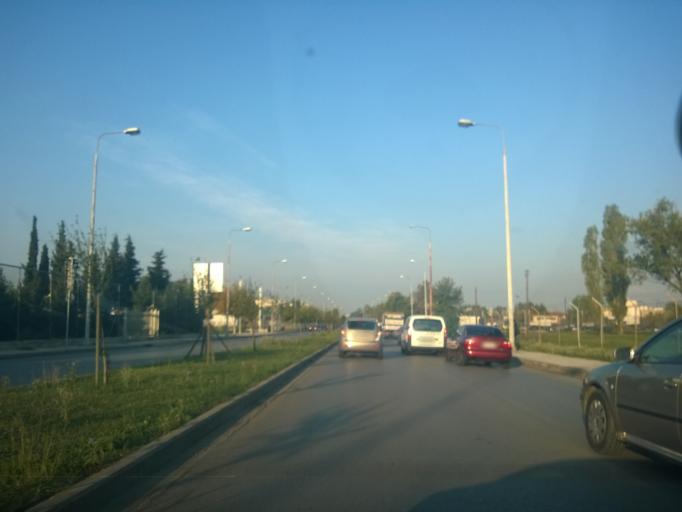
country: GR
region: Central Macedonia
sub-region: Nomos Thessalonikis
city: Evosmos
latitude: 40.6609
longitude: 22.9163
